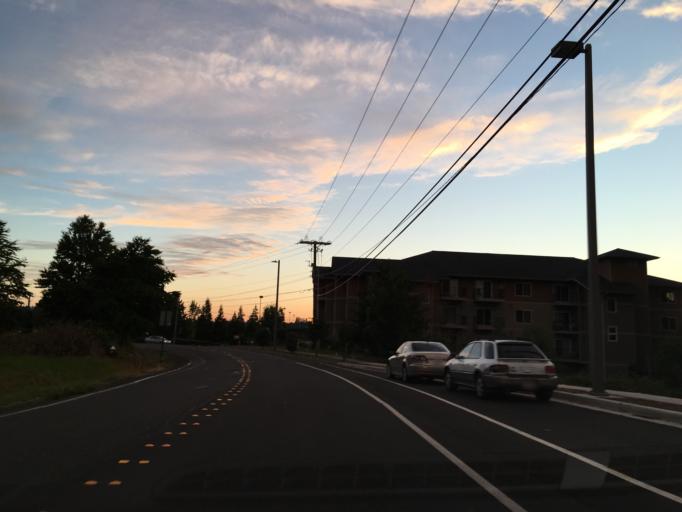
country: US
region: Washington
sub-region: Whatcom County
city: Bellingham
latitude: 48.7852
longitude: -122.4771
